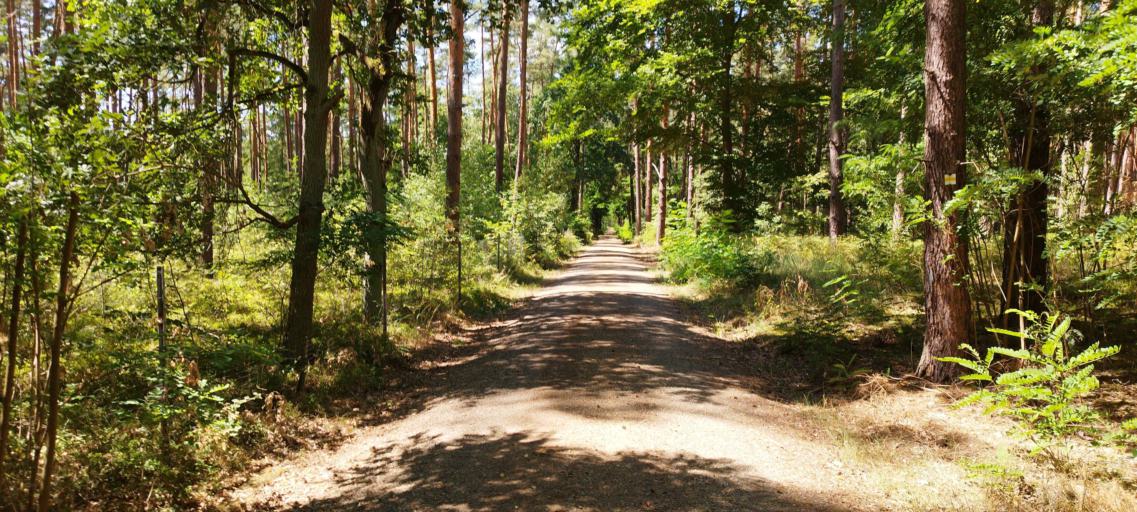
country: DE
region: Brandenburg
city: Reichenwalde
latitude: 52.2768
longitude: 13.9746
